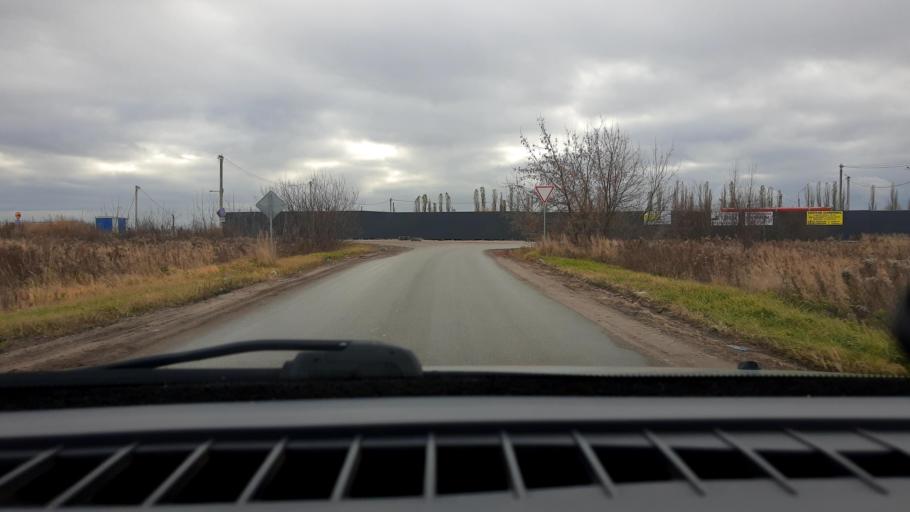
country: RU
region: Nizjnij Novgorod
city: Kstovo
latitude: 56.1946
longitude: 44.1390
